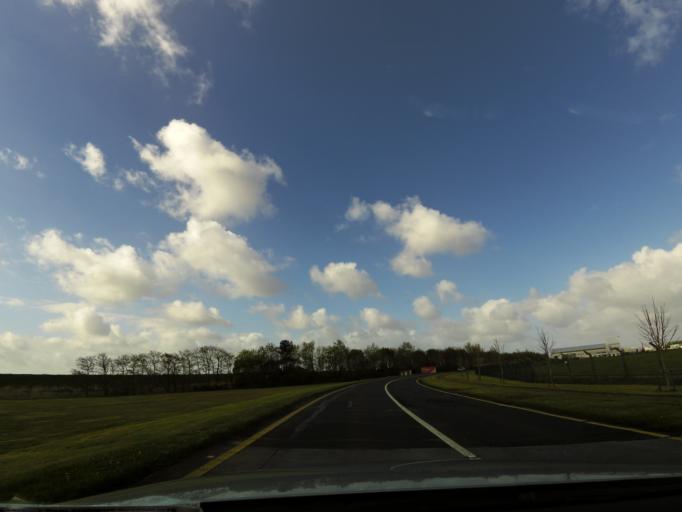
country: IE
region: Munster
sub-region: An Clar
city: Shannon
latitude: 52.6926
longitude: -8.9034
